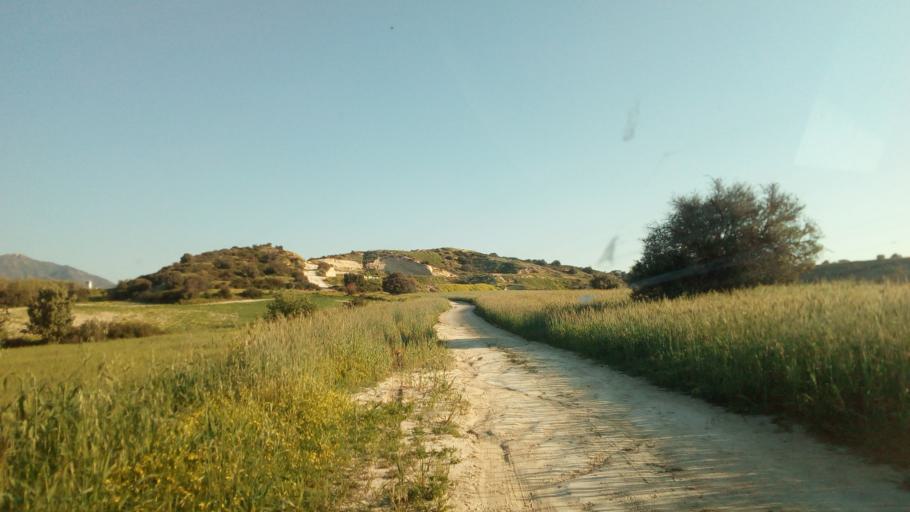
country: CY
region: Larnaka
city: Kofinou
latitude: 34.8409
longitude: 33.4486
